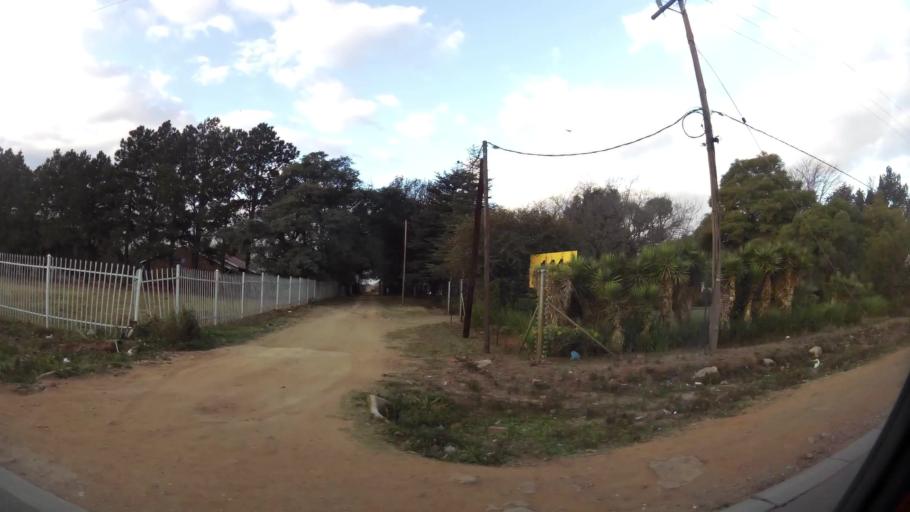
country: ZA
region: Gauteng
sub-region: City of Johannesburg Metropolitan Municipality
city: Midrand
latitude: -26.0110
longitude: 28.1614
